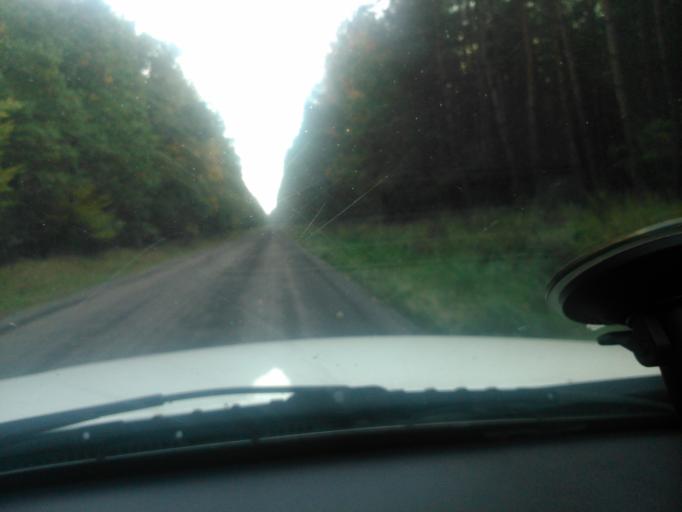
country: PL
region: Kujawsko-Pomorskie
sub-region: Powiat golubsko-dobrzynski
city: Golub-Dobrzyn
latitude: 53.1605
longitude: 19.1283
